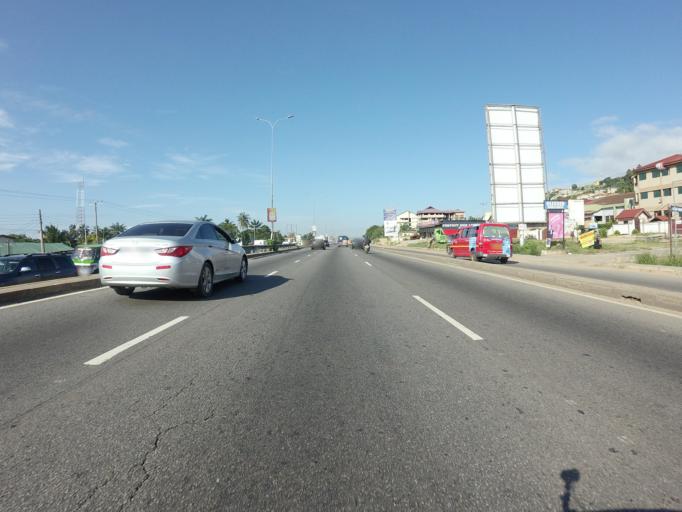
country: GH
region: Greater Accra
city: Gbawe
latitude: 5.5598
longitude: -0.2930
